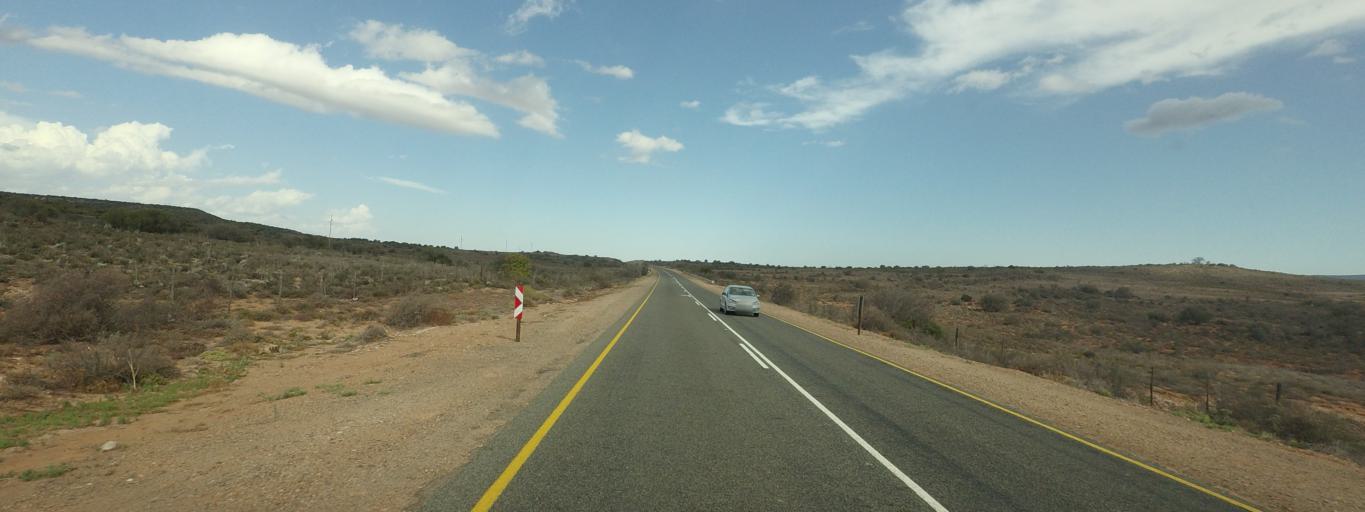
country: ZA
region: Western Cape
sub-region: Eden District Municipality
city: Oudtshoorn
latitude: -33.5674
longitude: 21.9188
